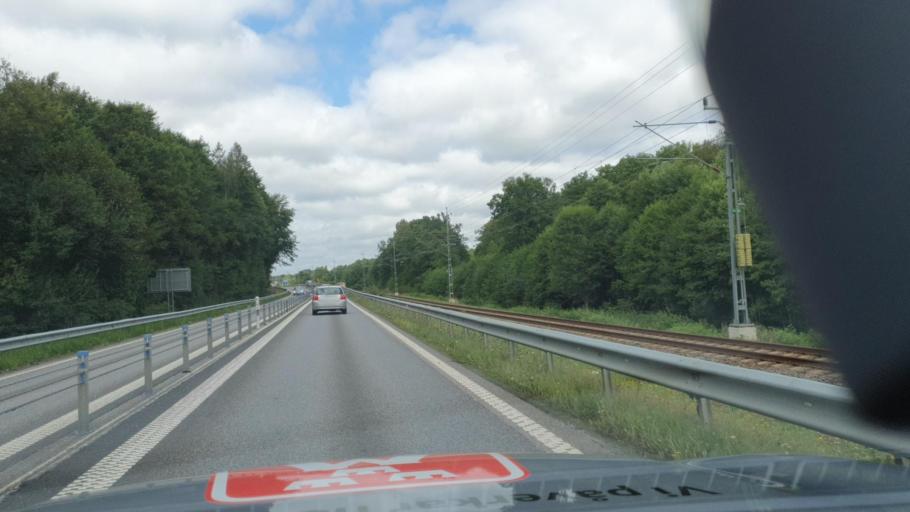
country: SE
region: Blekinge
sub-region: Karlskrona Kommun
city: Rodeby
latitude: 56.2430
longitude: 15.6254
